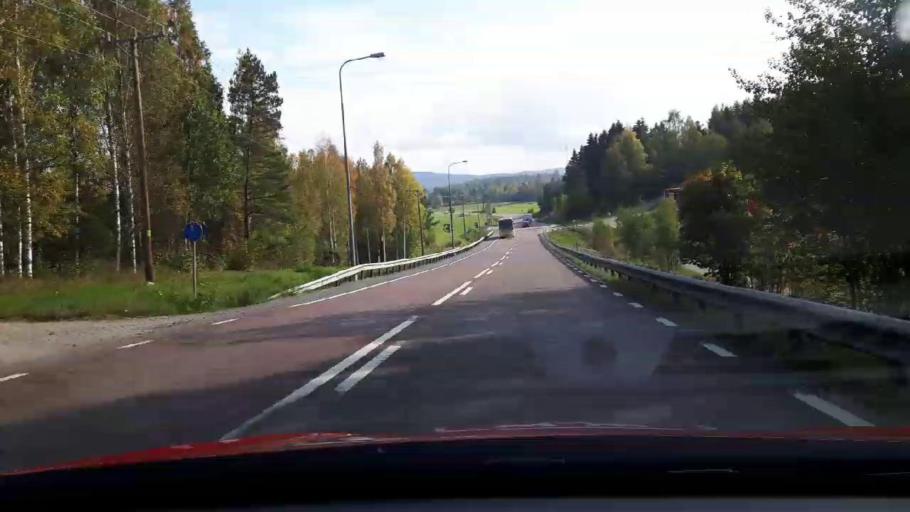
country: SE
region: Gaevleborg
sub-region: Bollnas Kommun
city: Kilafors
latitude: 61.2133
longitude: 16.6053
